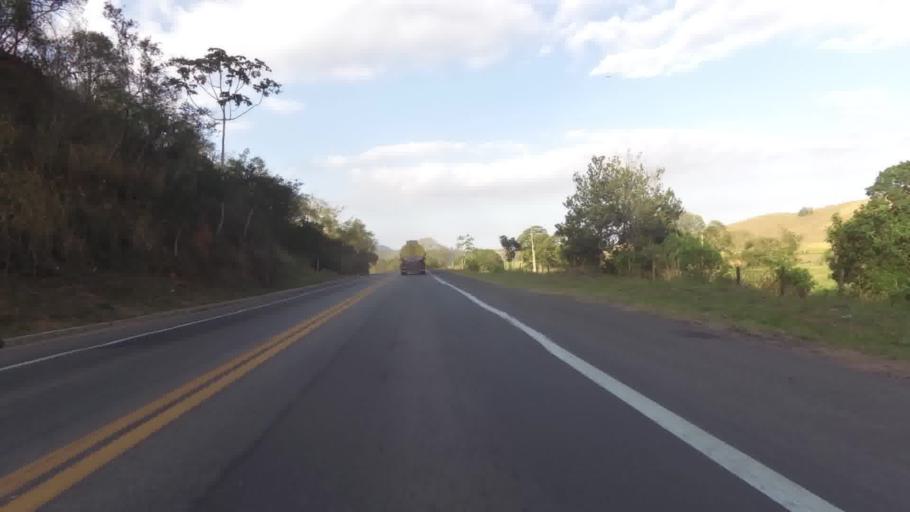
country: BR
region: Espirito Santo
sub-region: Cachoeiro De Itapemirim
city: Cachoeiro de Itapemirim
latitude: -20.9074
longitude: -41.0679
